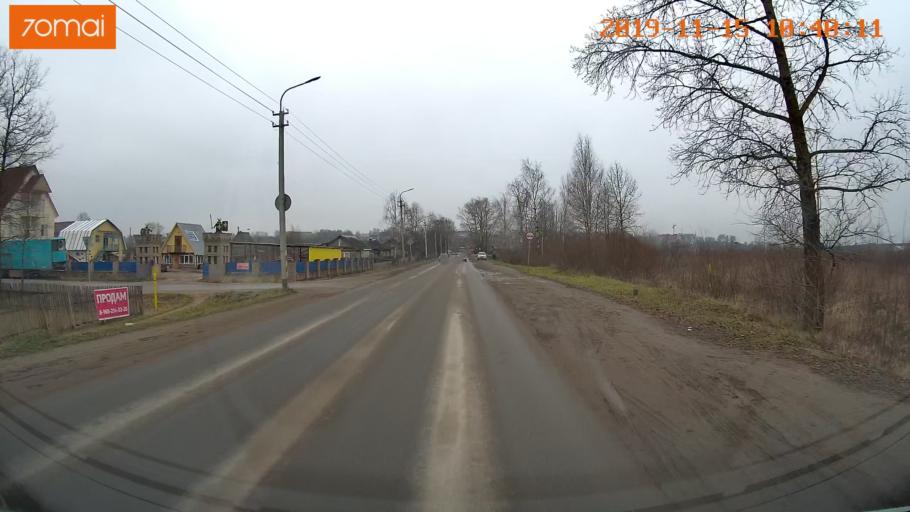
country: RU
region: Vologda
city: Sheksna
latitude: 59.2161
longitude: 38.5099
